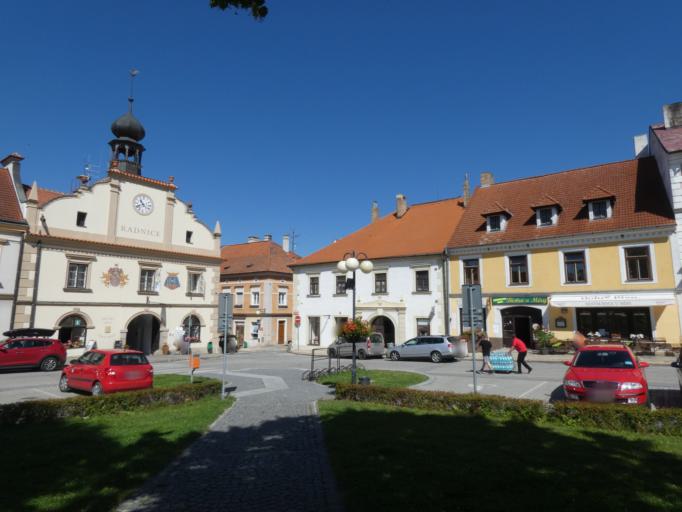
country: CZ
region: Jihocesky
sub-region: Okres Ceske Budejovice
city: Nove Hrady
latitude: 48.7901
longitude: 14.7785
